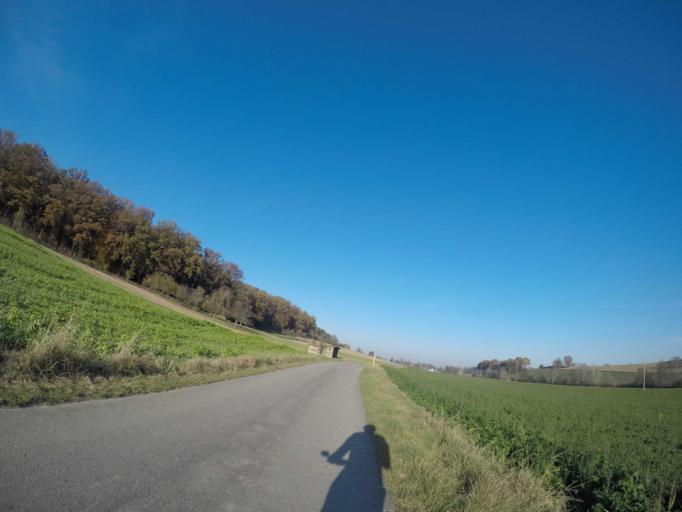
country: DE
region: Baden-Wuerttemberg
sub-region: Tuebingen Region
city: Grundsheim
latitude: 48.1816
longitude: 9.6683
